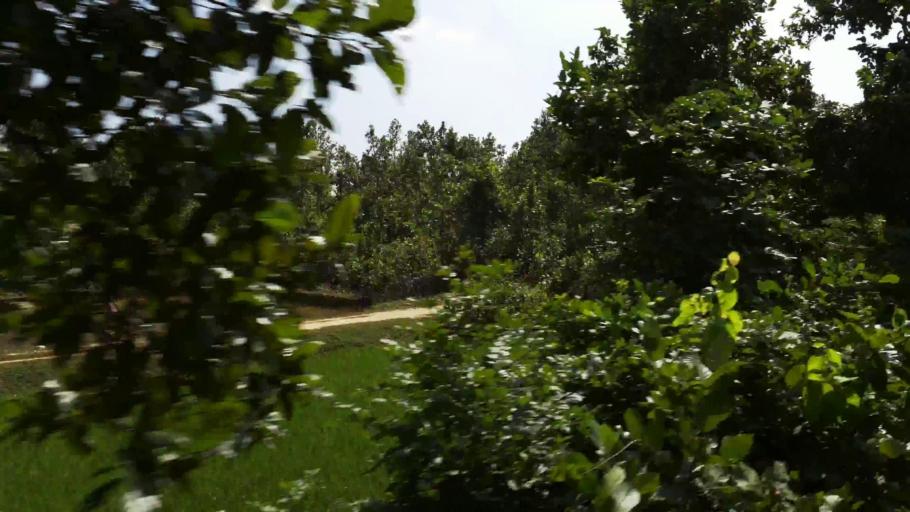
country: BD
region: Dhaka
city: Tungi
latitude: 24.1611
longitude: 90.4681
